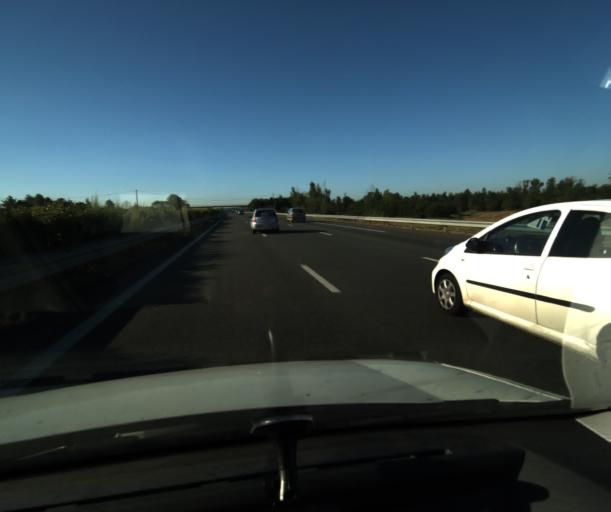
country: FR
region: Midi-Pyrenees
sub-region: Departement du Tarn-et-Garonne
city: Campsas
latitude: 43.8755
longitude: 1.3172
